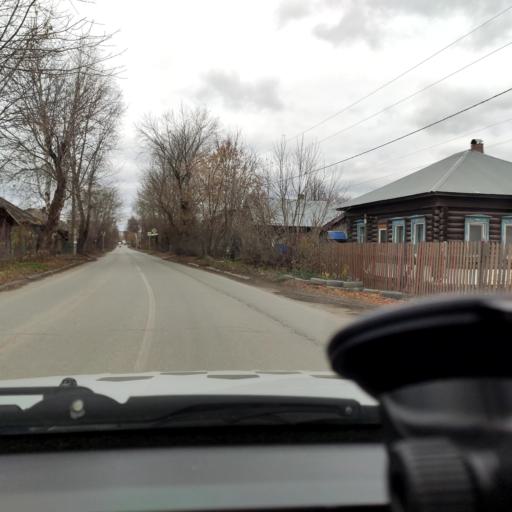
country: RU
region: Perm
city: Perm
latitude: 58.0131
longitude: 56.3198
